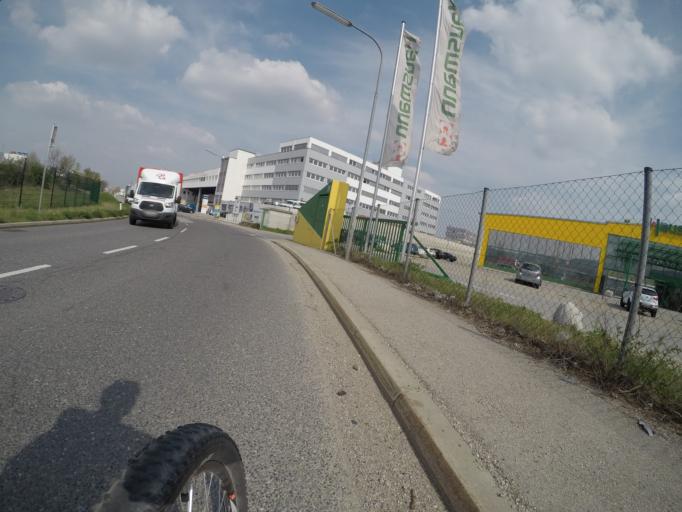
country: AT
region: Lower Austria
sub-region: Politischer Bezirk Modling
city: Wiener Neudorf
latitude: 48.0734
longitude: 16.3098
